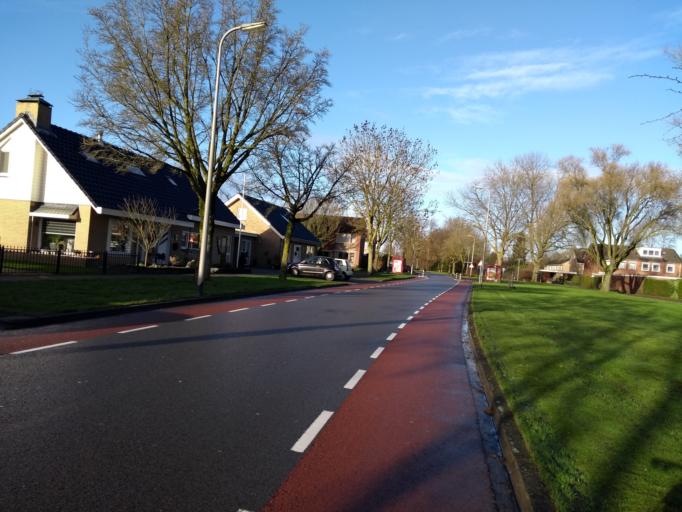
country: NL
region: Overijssel
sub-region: Gemeente Wierden
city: Wierden
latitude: 52.3599
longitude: 6.6010
